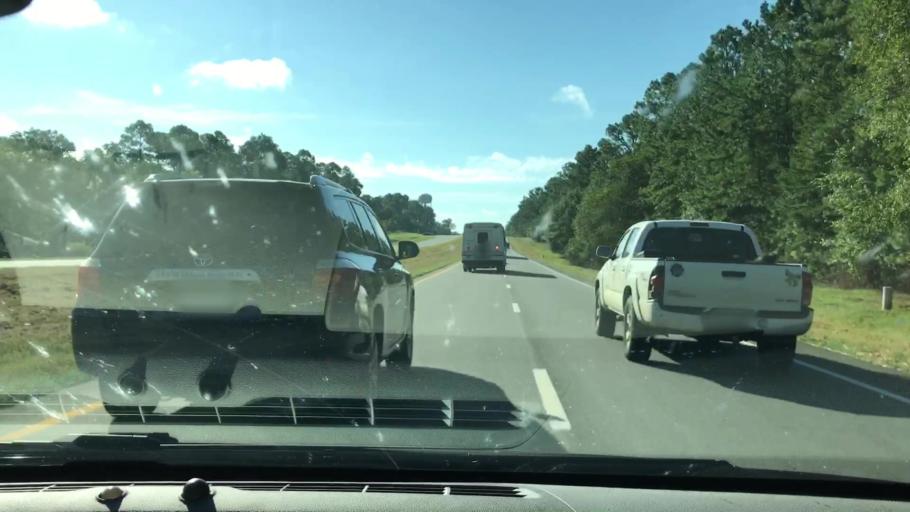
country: US
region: Georgia
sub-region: Dougherty County
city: Albany
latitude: 31.6454
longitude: -84.2579
